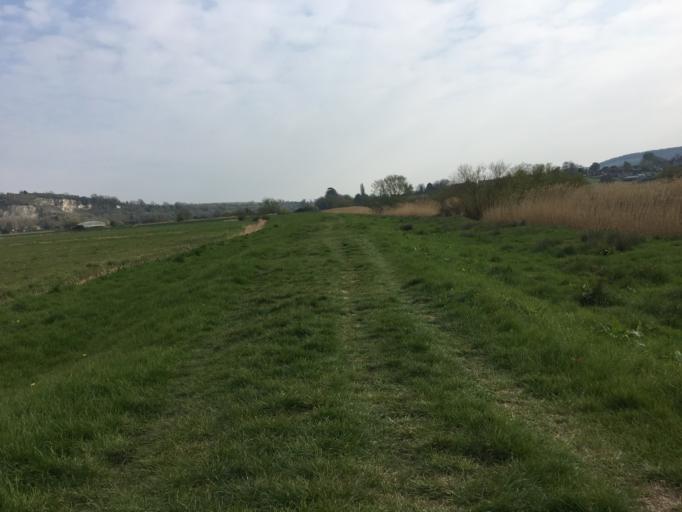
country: GB
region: England
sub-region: West Sussex
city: Arundel
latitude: 50.9016
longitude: -0.5527
